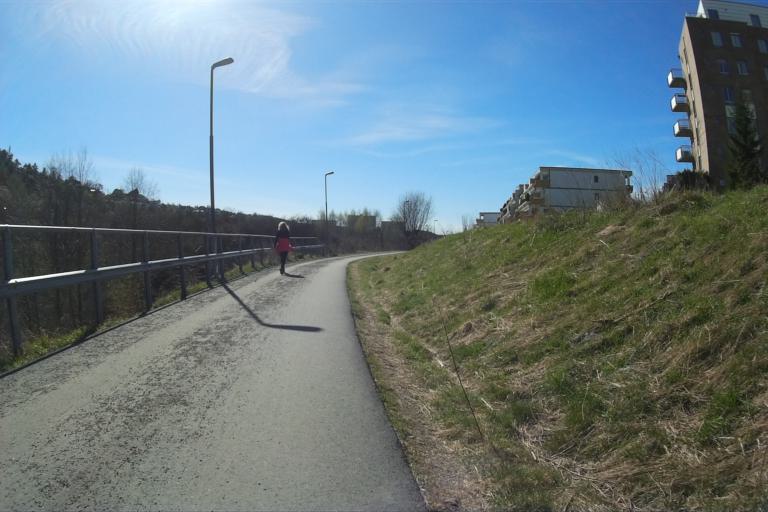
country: NO
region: Oslo
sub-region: Oslo
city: Oslo
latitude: 59.9077
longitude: 10.8079
